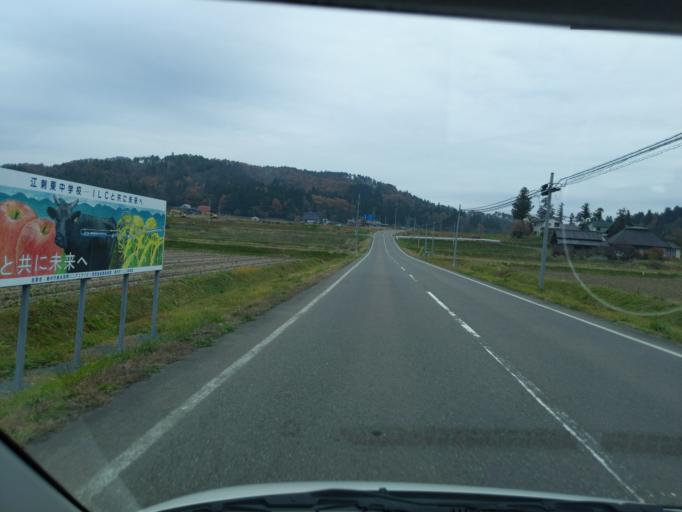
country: JP
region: Iwate
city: Kitakami
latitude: 39.2203
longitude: 141.2236
